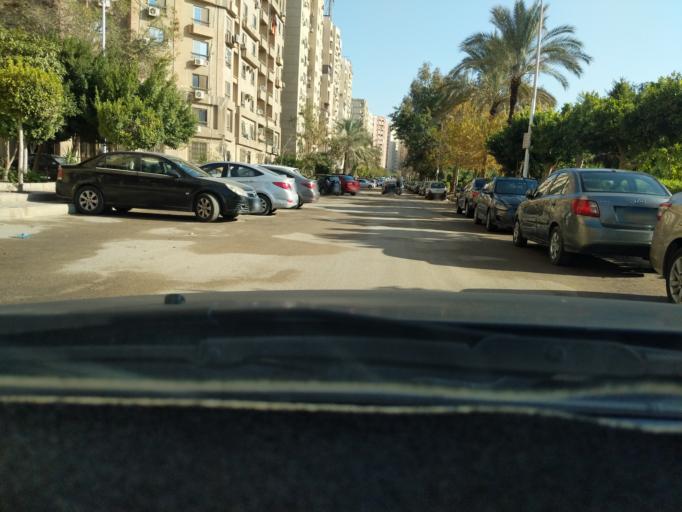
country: EG
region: Al Jizah
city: Al Hawamidiyah
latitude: 29.9626
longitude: 31.3184
